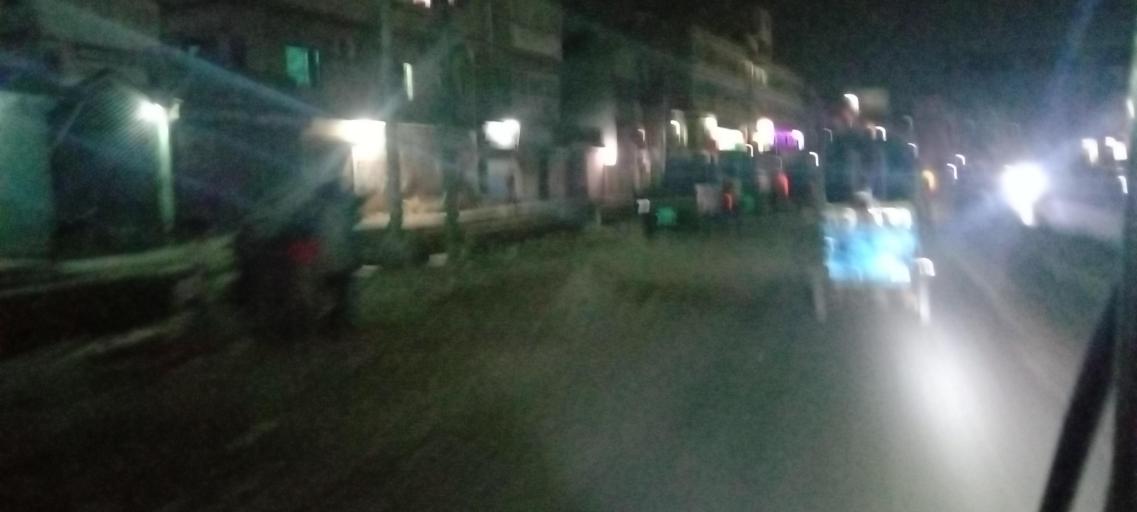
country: BD
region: Dhaka
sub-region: Dhaka
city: Dhaka
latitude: 23.7011
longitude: 90.3960
